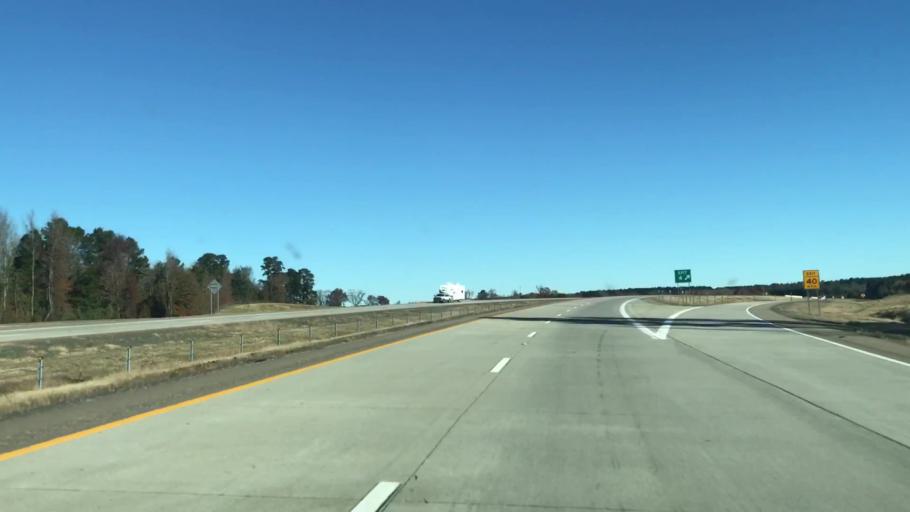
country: US
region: Louisiana
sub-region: Caddo Parish
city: Vivian
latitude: 33.0753
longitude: -93.9041
